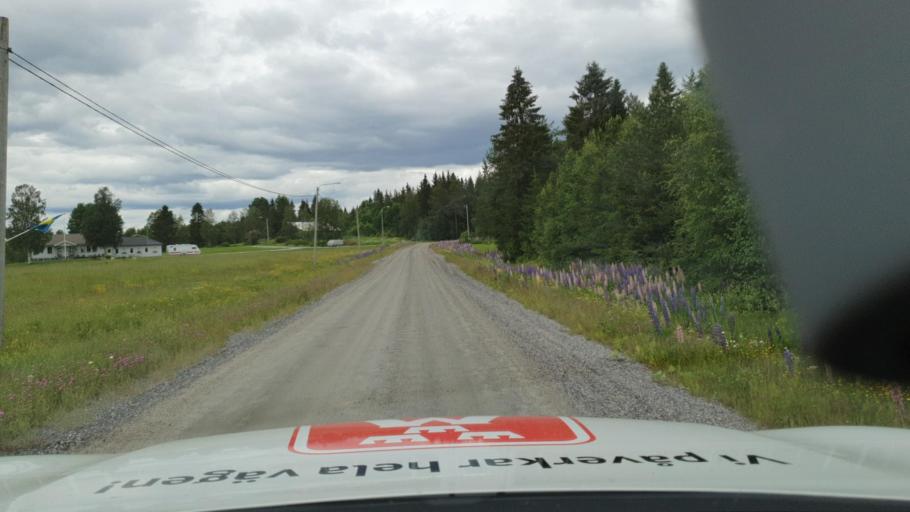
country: SE
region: Vaesterbotten
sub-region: Bjurholms Kommun
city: Bjurholm
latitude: 63.7612
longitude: 19.2630
